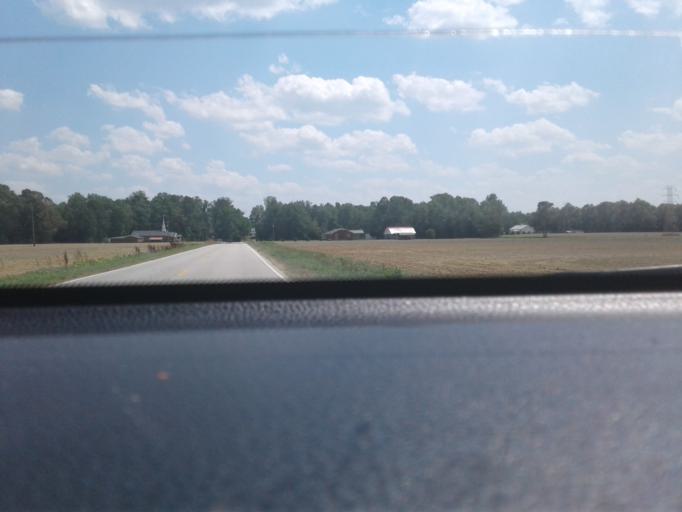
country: US
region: North Carolina
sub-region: Harnett County
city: Erwin
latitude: 35.2853
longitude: -78.6718
